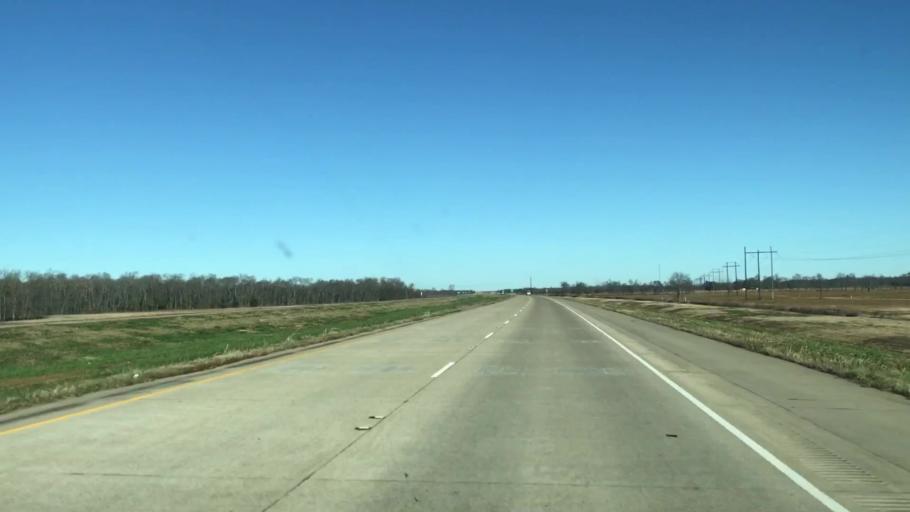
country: US
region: Louisiana
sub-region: Caddo Parish
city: Blanchard
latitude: 32.6540
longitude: -93.8416
